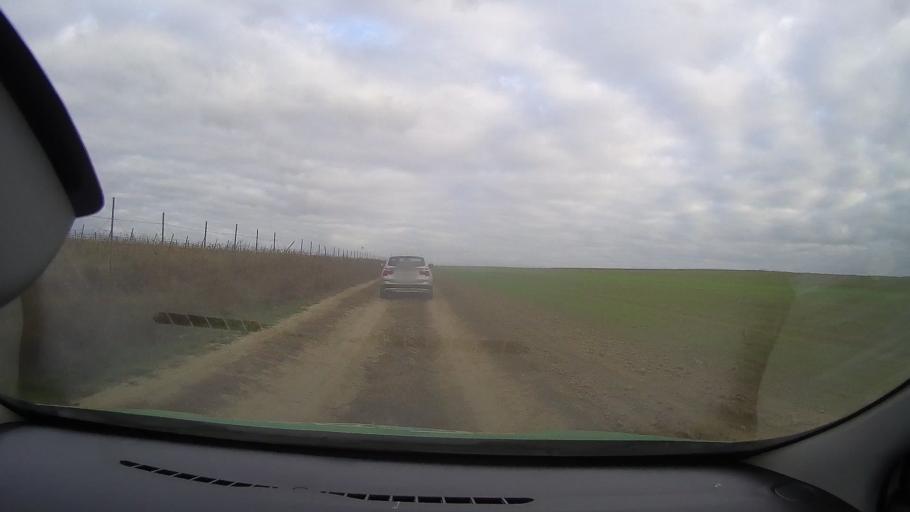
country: RO
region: Tulcea
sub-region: Comuna Jurilovca
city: Jurilovca
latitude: 44.7657
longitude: 28.9069
